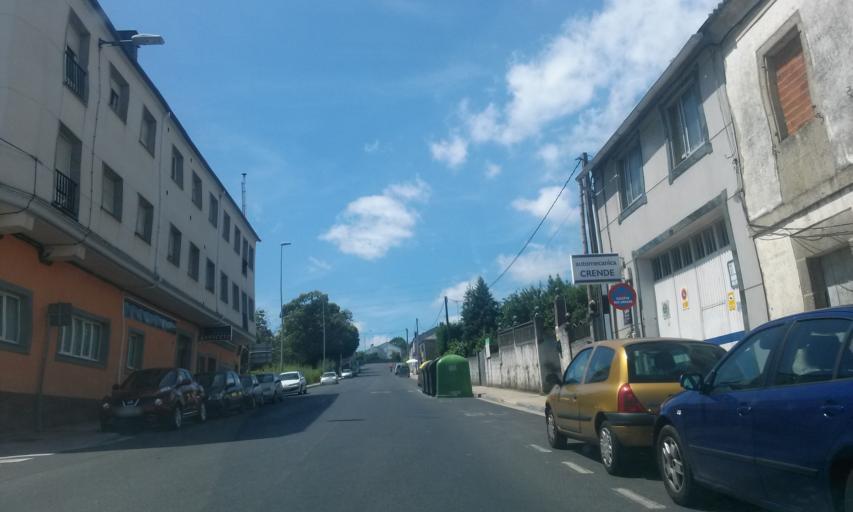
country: ES
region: Galicia
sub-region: Provincia de Lugo
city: Lugo
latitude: 42.9963
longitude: -7.5672
